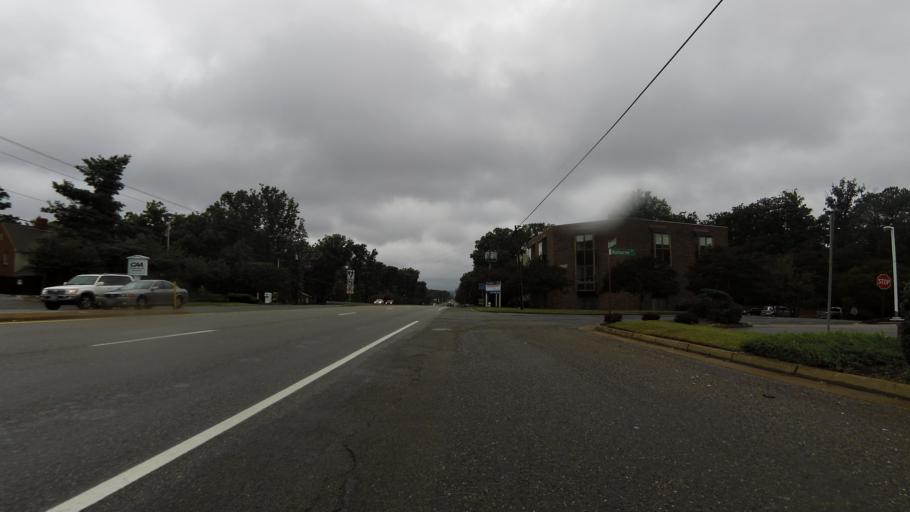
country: US
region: Virginia
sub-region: Henrico County
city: Tuckahoe
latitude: 37.5948
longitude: -77.5668
